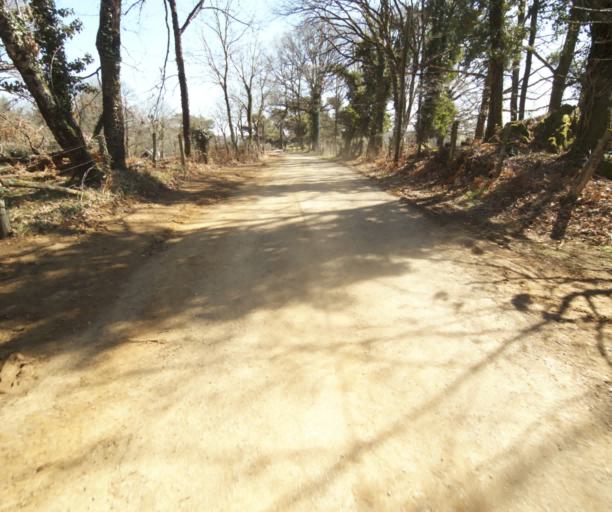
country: FR
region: Limousin
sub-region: Departement de la Correze
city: Saint-Clement
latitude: 45.3711
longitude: 1.6840
